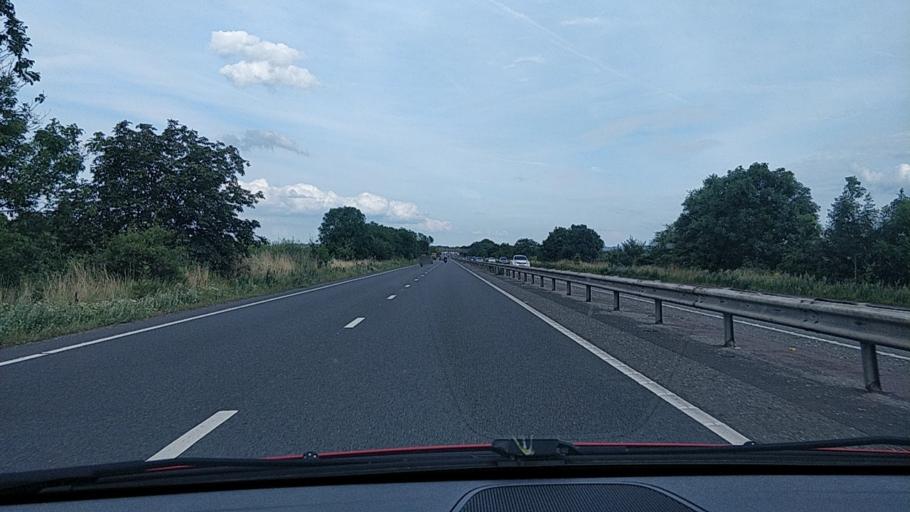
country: GB
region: Wales
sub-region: Wrexham
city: Rossett
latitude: 53.1601
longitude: -2.9506
